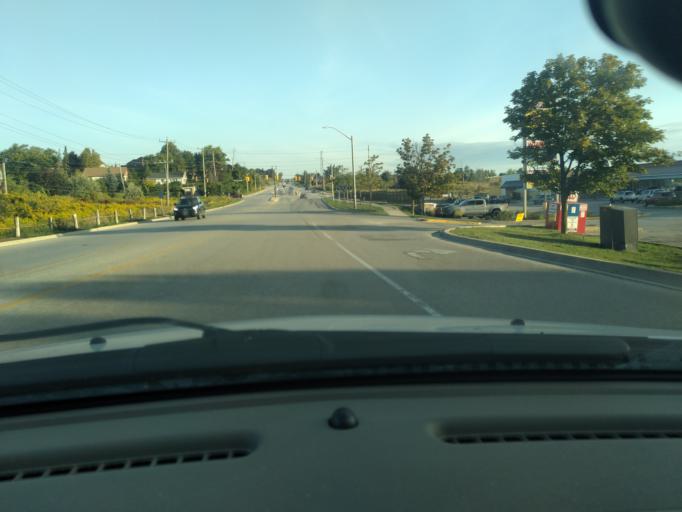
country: CA
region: Ontario
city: Bradford West Gwillimbury
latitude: 44.1250
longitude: -79.5675
